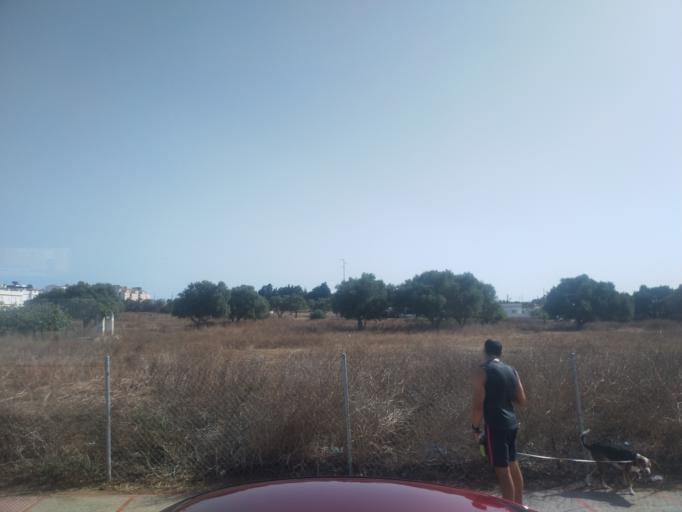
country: ES
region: Andalusia
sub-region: Provincia de Cadiz
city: San Fernando
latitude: 36.4483
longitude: -6.2172
